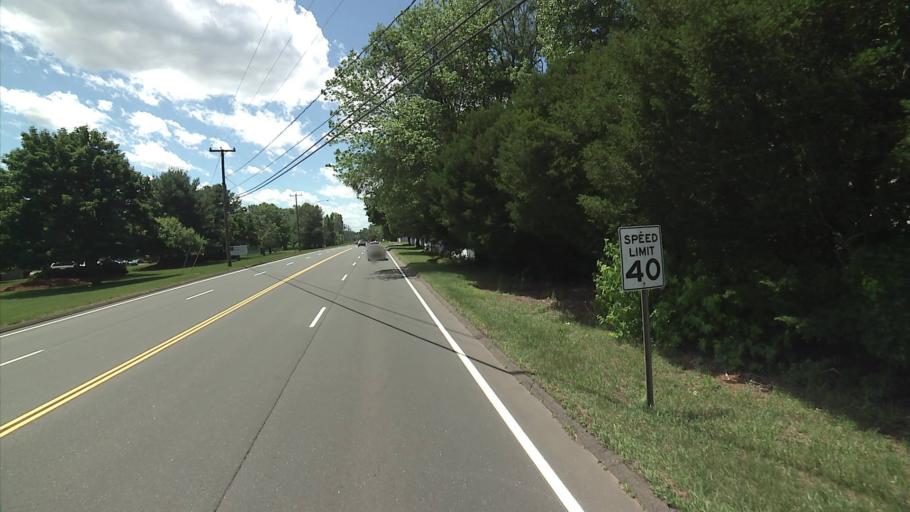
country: US
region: Connecticut
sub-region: Hartford County
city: Sherwood Manor
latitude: 42.0060
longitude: -72.5556
